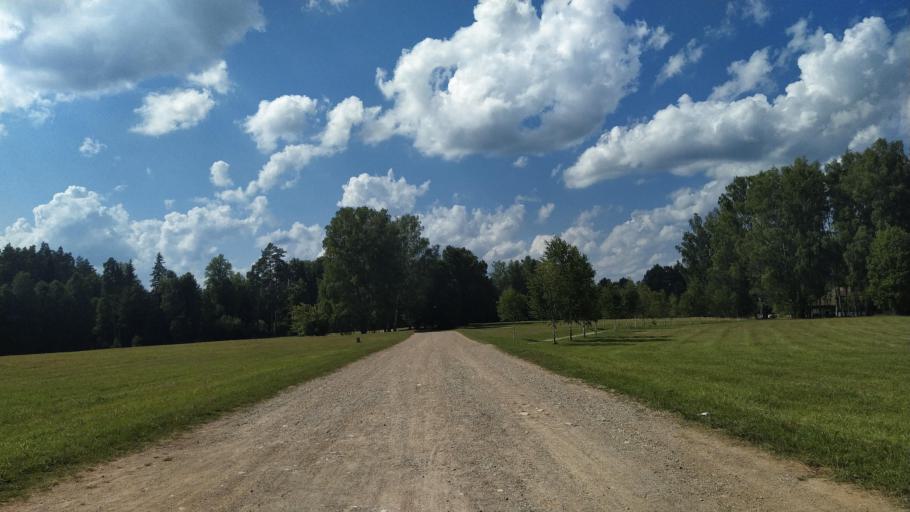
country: RU
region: Pskov
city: Pushkinskiye Gory
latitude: 57.0598
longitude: 28.9278
